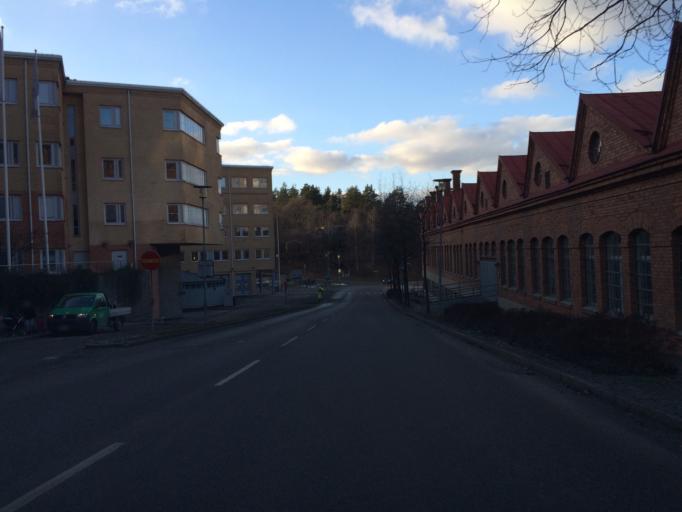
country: SE
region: Stockholm
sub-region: Nacka Kommun
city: Nacka
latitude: 59.3152
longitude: 18.1623
